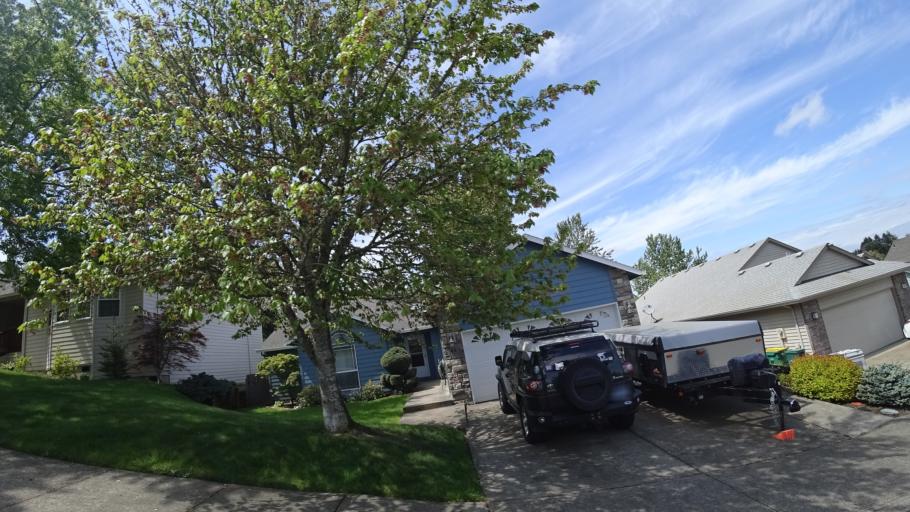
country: US
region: Oregon
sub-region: Washington County
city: Aloha
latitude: 45.4658
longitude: -122.8898
